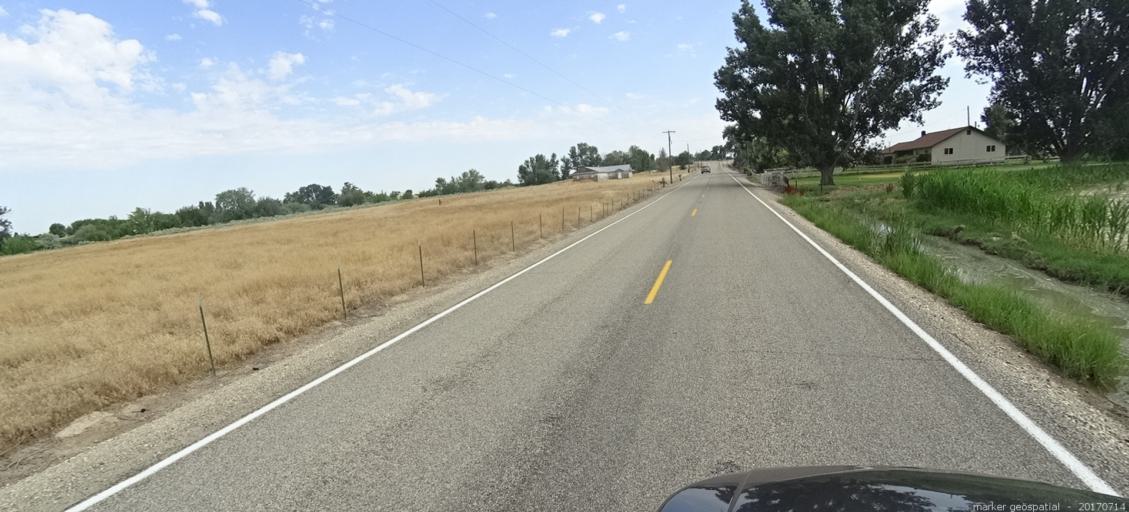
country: US
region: Idaho
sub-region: Ada County
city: Kuna
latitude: 43.4818
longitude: -116.3544
